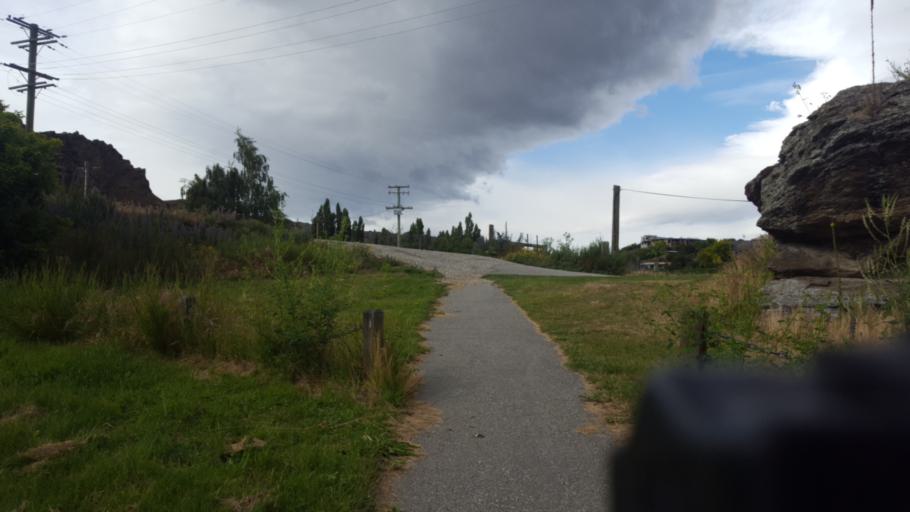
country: NZ
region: Otago
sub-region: Queenstown-Lakes District
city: Wanaka
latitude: -45.2544
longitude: 169.3994
